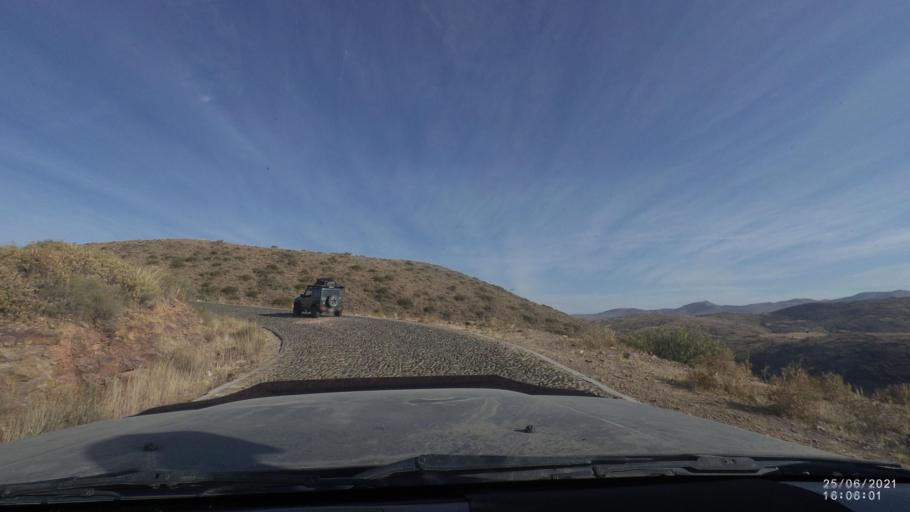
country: BO
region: Cochabamba
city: Cliza
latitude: -17.6659
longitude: -65.9092
